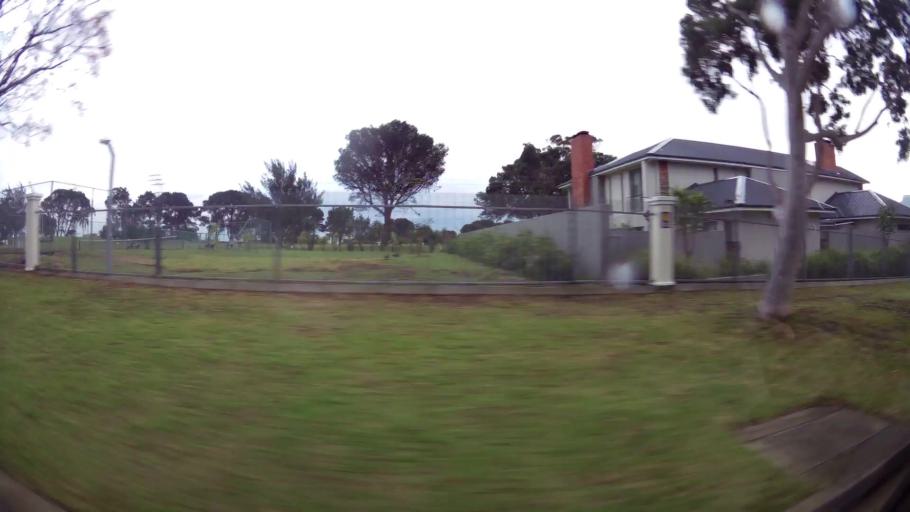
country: ZA
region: Eastern Cape
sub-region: Nelson Mandela Bay Metropolitan Municipality
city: Port Elizabeth
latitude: -33.9744
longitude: 25.5782
